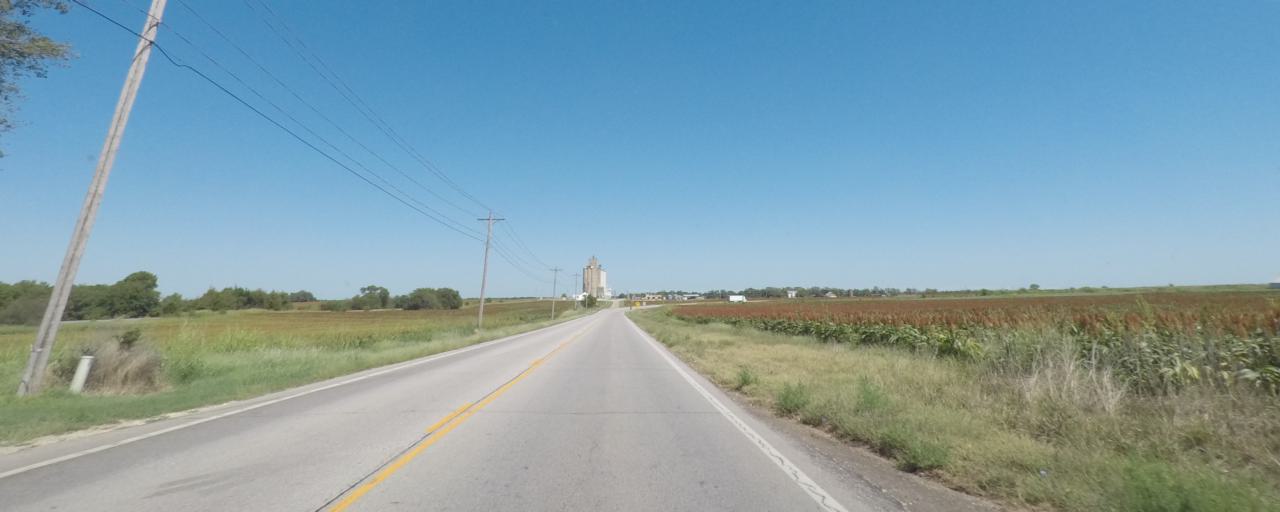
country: US
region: Kansas
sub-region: Sumner County
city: Wellington
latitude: 37.2970
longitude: -97.3940
